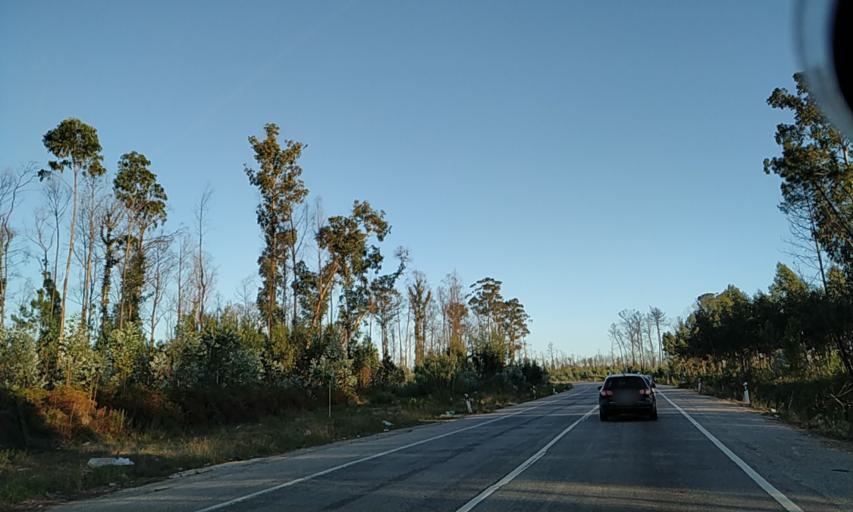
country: PT
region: Aveiro
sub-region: Oliveira do Bairro
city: Oia
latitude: 40.5621
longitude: -8.5634
